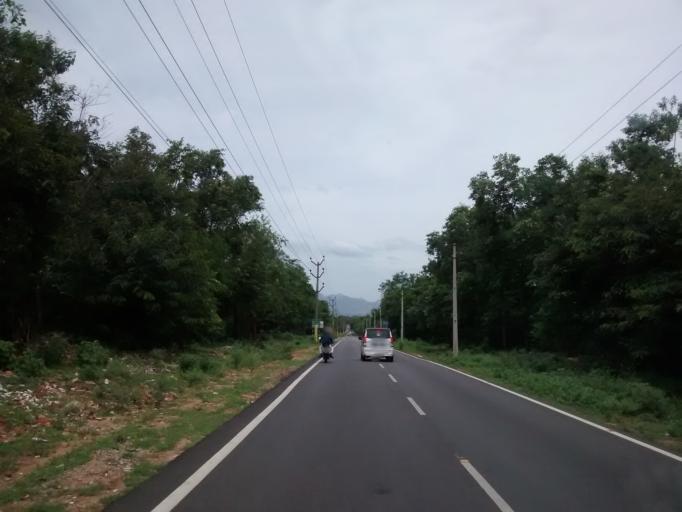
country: IN
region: Andhra Pradesh
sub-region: Chittoor
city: Tirupati
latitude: 13.6390
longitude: 79.3957
